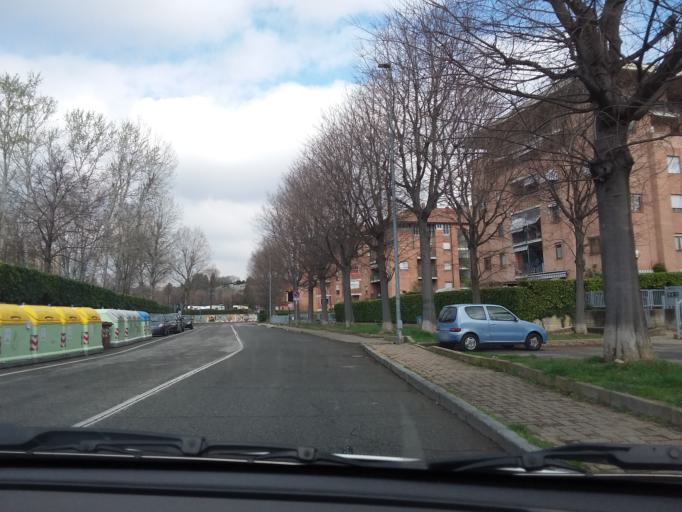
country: IT
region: Piedmont
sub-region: Provincia di Torino
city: Rivoli
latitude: 45.0637
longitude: 7.5278
